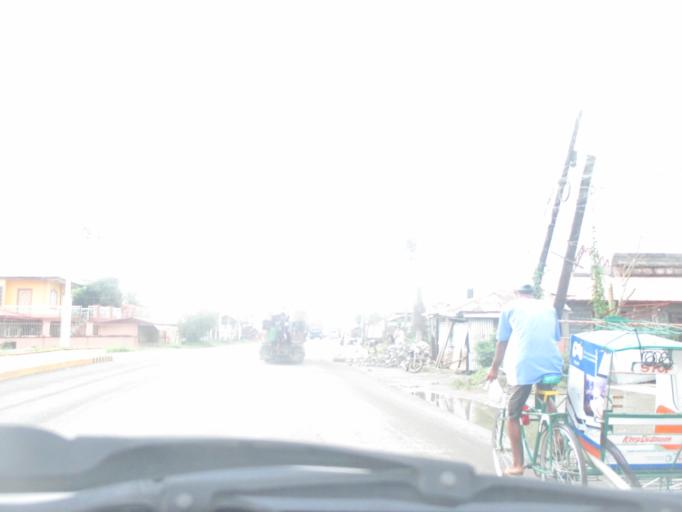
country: PH
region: Eastern Visayas
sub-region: Province of Leyte
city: Panalanoy
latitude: 11.2451
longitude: 124.9830
